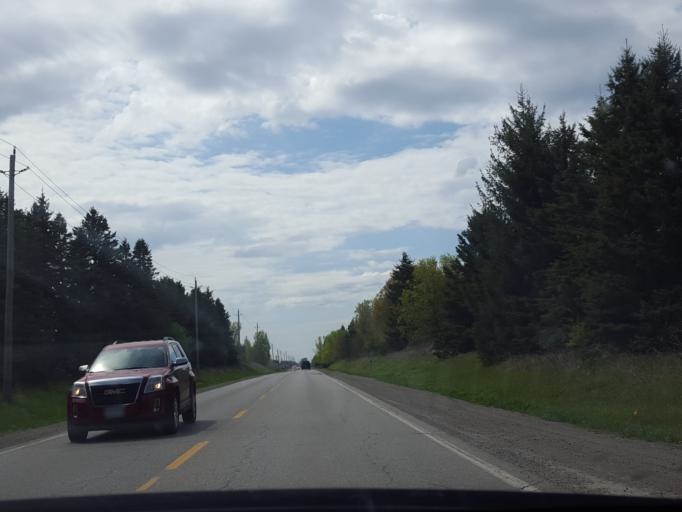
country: CA
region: Ontario
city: Oshawa
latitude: 43.9451
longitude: -78.7172
